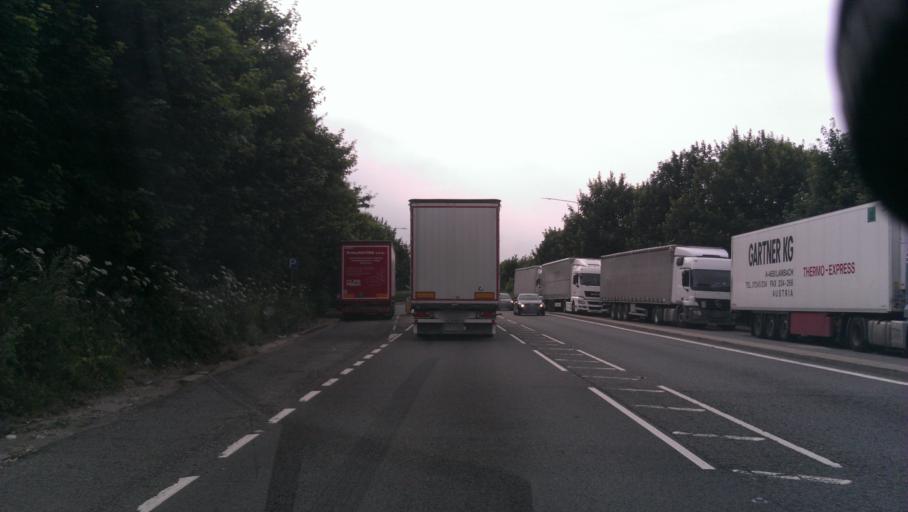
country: GB
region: England
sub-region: Kent
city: Dover
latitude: 51.1479
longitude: 1.3256
